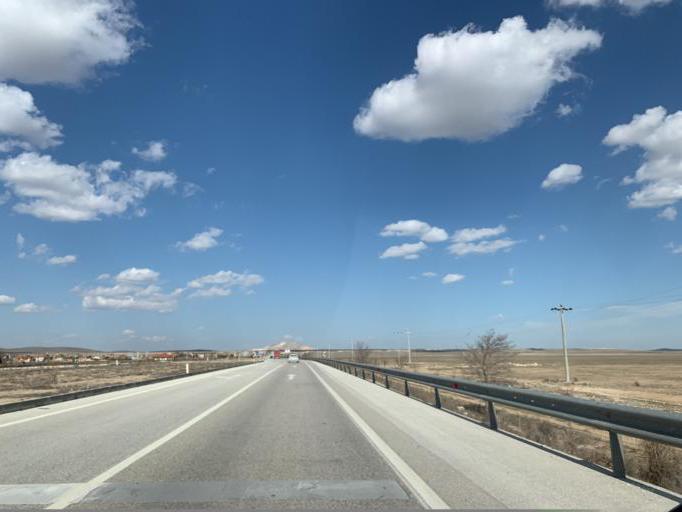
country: TR
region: Konya
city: Cihanbeyli
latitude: 38.5107
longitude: 32.8546
